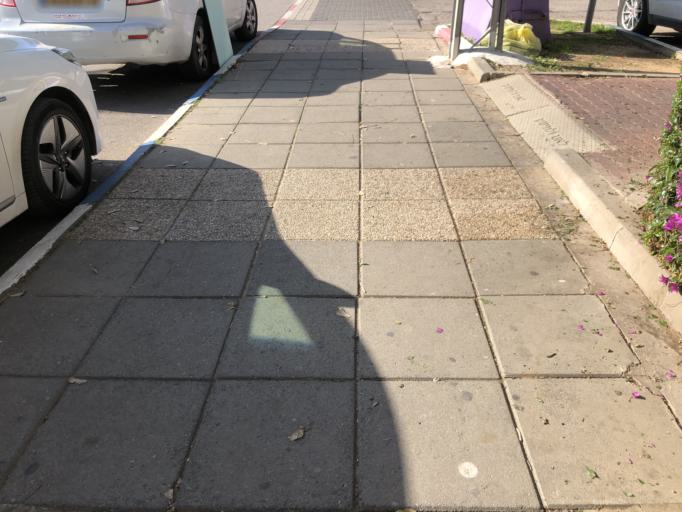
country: IL
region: Central District
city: Kfar Saba
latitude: 32.1760
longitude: 34.9104
